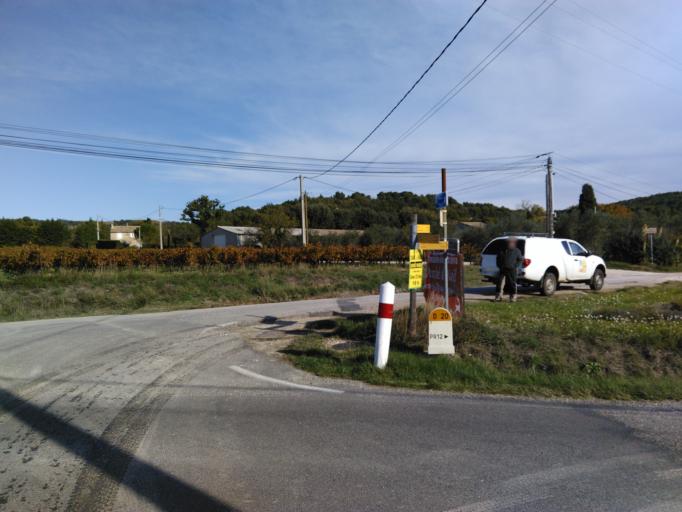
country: FR
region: Provence-Alpes-Cote d'Azur
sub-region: Departement du Vaucluse
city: Visan
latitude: 44.3050
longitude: 4.9724
